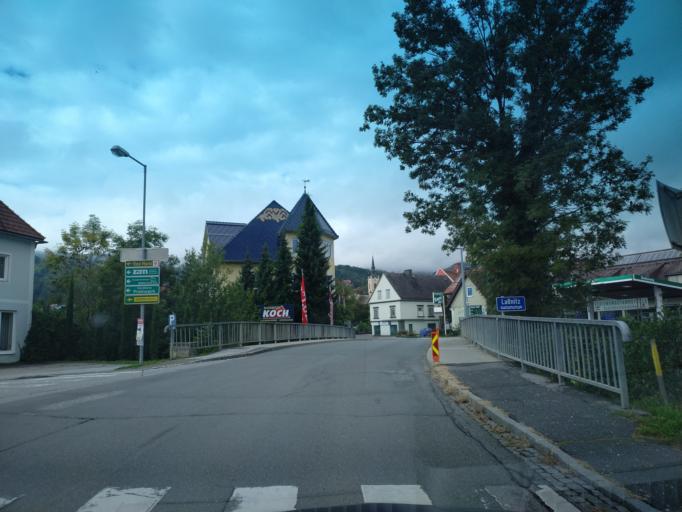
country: AT
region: Styria
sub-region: Politischer Bezirk Deutschlandsberg
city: Deutschlandsberg
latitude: 46.8151
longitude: 15.2186
